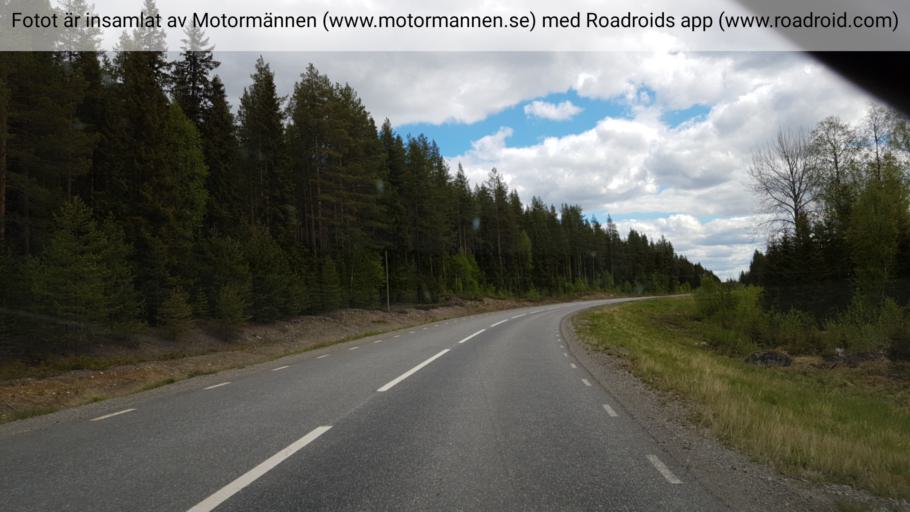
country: SE
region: Vaesterbotten
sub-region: Norsjo Kommun
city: Norsjoe
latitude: 64.8921
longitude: 19.5942
